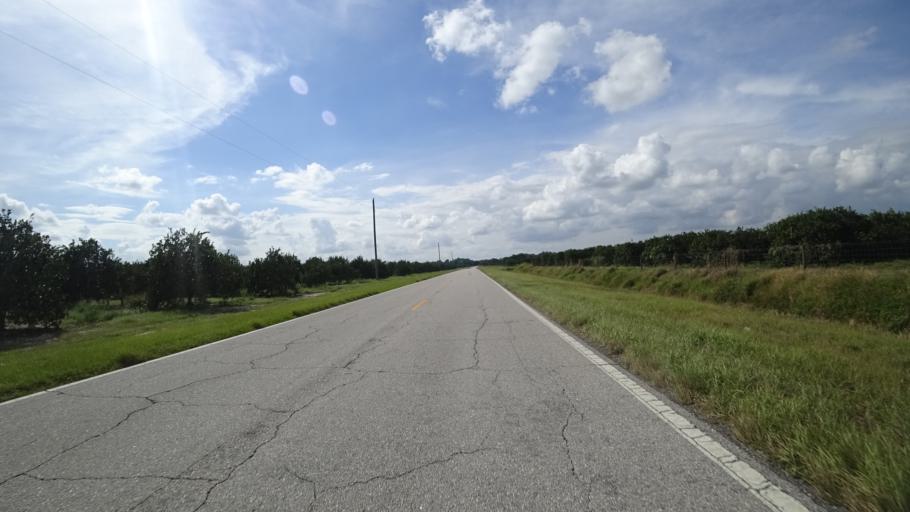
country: US
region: Florida
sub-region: Hillsborough County
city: Wimauma
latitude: 27.5373
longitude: -82.0943
